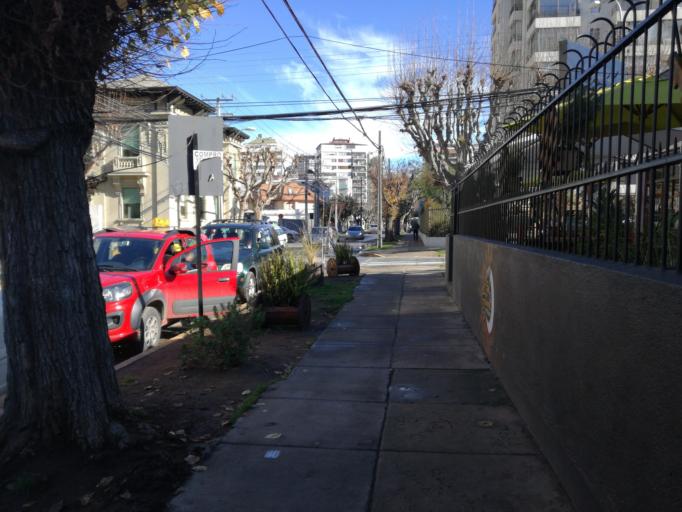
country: CL
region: Valparaiso
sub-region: Provincia de Valparaiso
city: Vina del Mar
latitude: -33.0219
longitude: -71.5485
